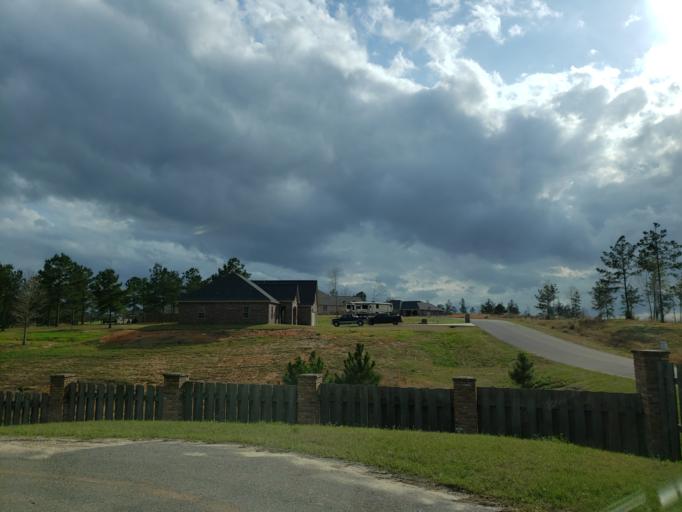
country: US
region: Mississippi
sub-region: Jones County
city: Ellisville
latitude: 31.5576
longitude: -89.2561
